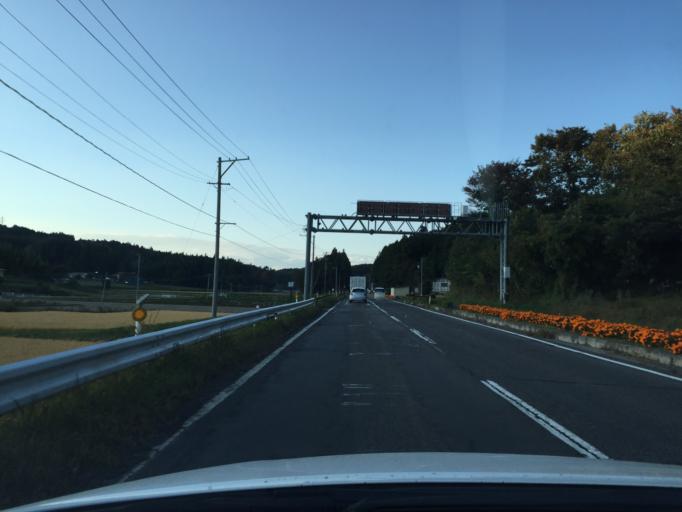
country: JP
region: Fukushima
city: Ishikawa
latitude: 37.2614
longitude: 140.5566
